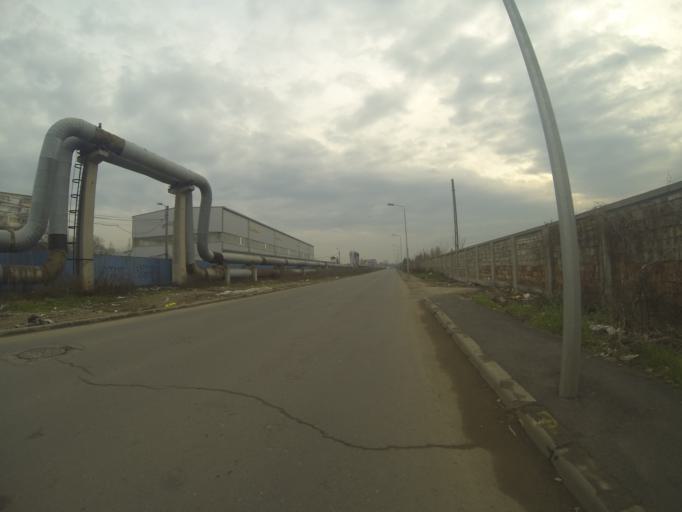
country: RO
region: Bucuresti
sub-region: Municipiul Bucuresti
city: Bucuresti
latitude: 44.3847
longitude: 26.0867
